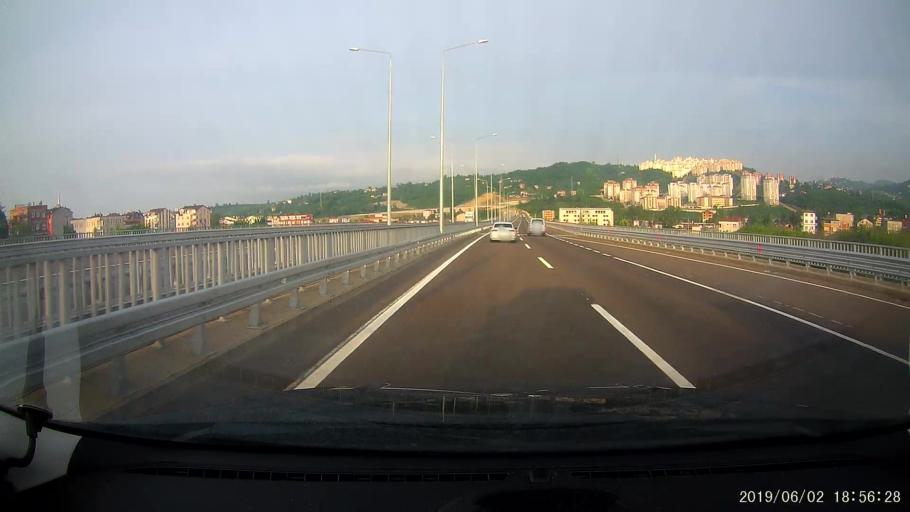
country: TR
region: Ordu
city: Ordu
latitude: 40.9558
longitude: 37.8915
